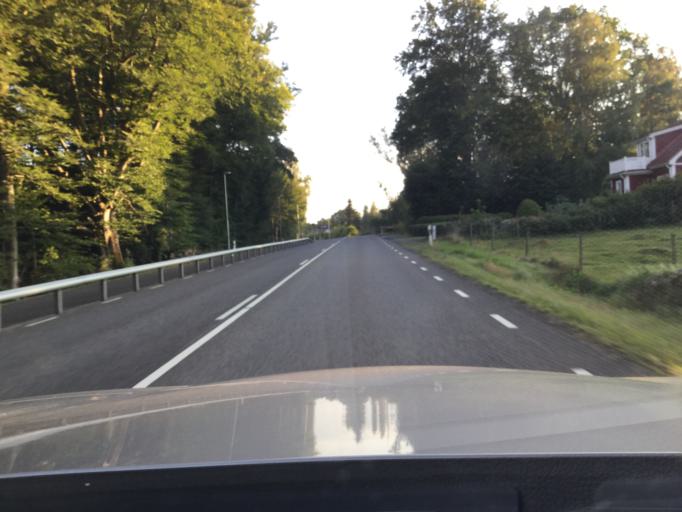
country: SE
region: Kronoberg
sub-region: Almhults Kommun
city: AElmhult
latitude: 56.6615
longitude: 14.2543
